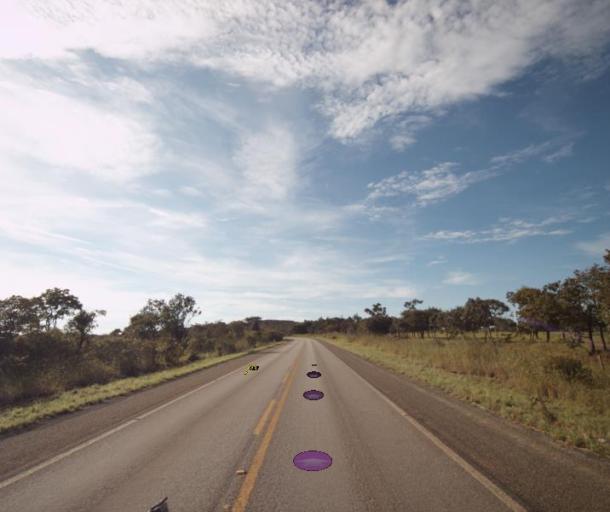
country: BR
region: Goias
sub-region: Pirenopolis
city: Pirenopolis
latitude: -15.7691
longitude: -48.5648
